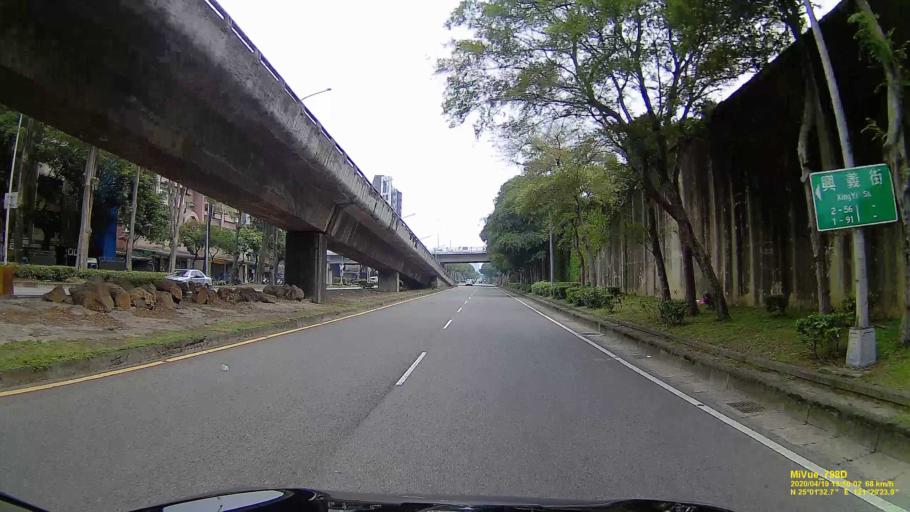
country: TW
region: Taipei
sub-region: Taipei
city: Banqiao
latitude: 25.0254
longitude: 121.4901
